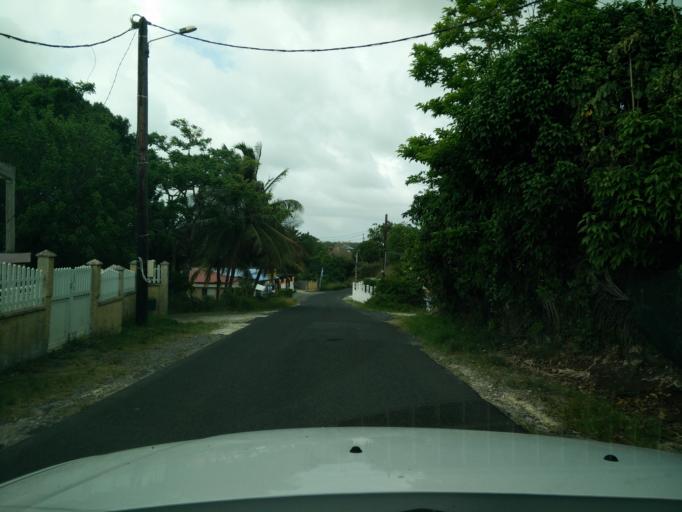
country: GP
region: Guadeloupe
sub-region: Guadeloupe
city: Le Gosier
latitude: 16.2409
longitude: -61.4442
